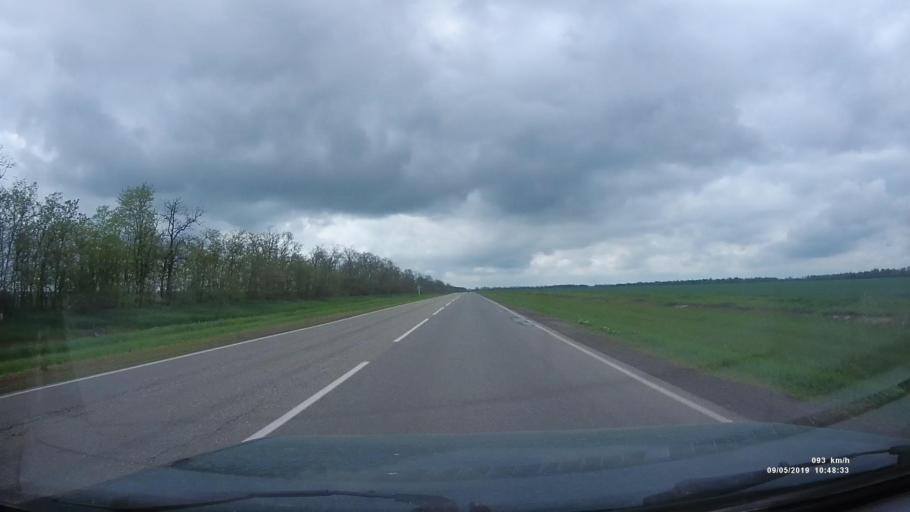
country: RU
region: Rostov
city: Peshkovo
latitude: 46.9549
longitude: 39.3556
